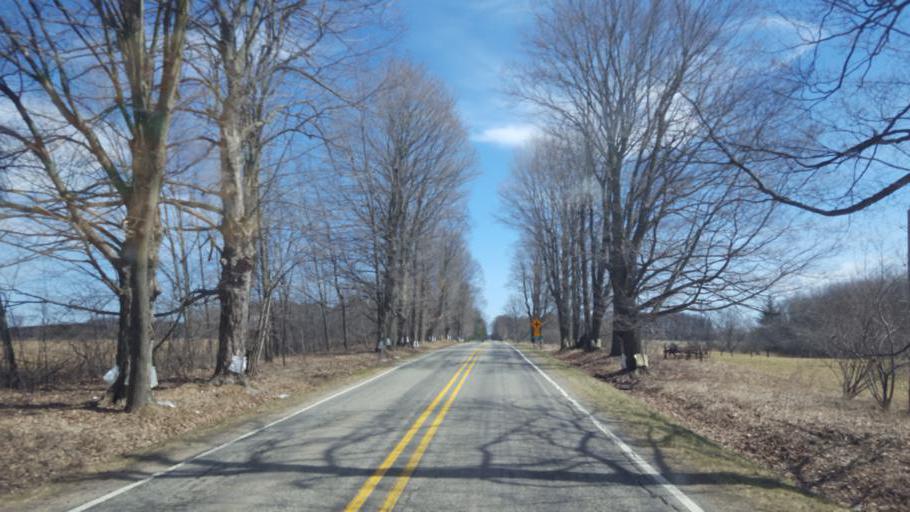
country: US
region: Michigan
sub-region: Montcalm County
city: Edmore
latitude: 43.5237
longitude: -85.0298
